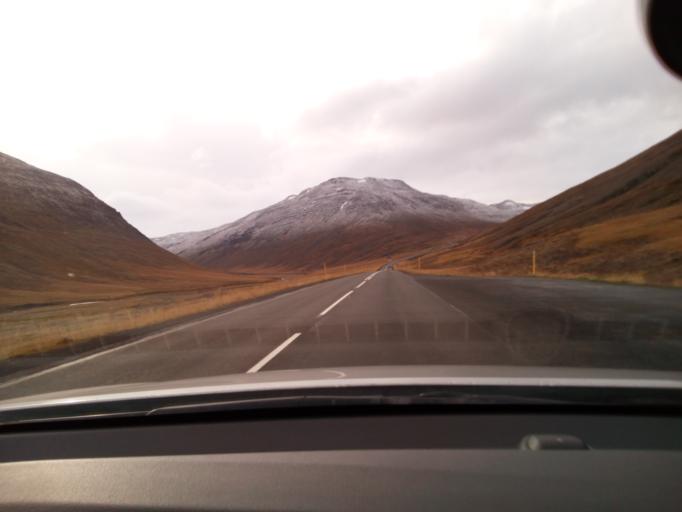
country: IS
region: Northeast
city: Dalvik
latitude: 65.4861
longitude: -18.6480
